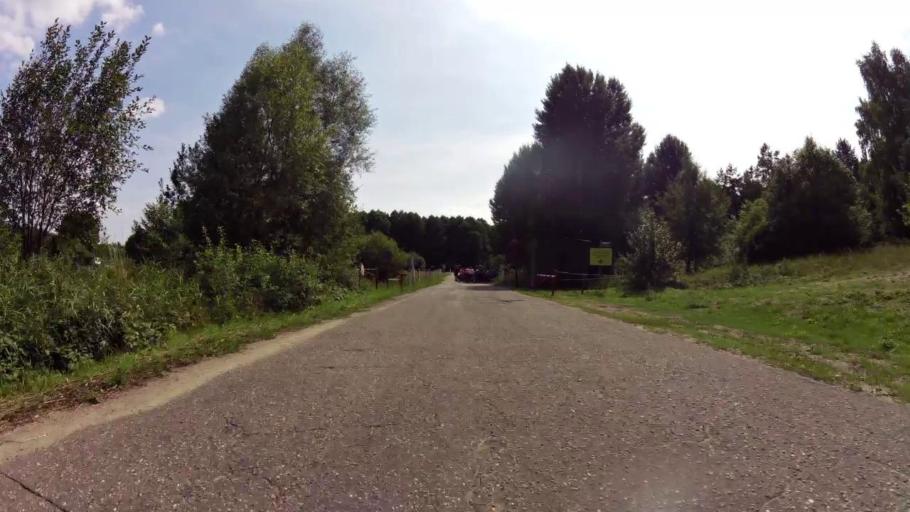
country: PL
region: West Pomeranian Voivodeship
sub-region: Powiat choszczenski
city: Drawno
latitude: 53.3182
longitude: 15.6867
